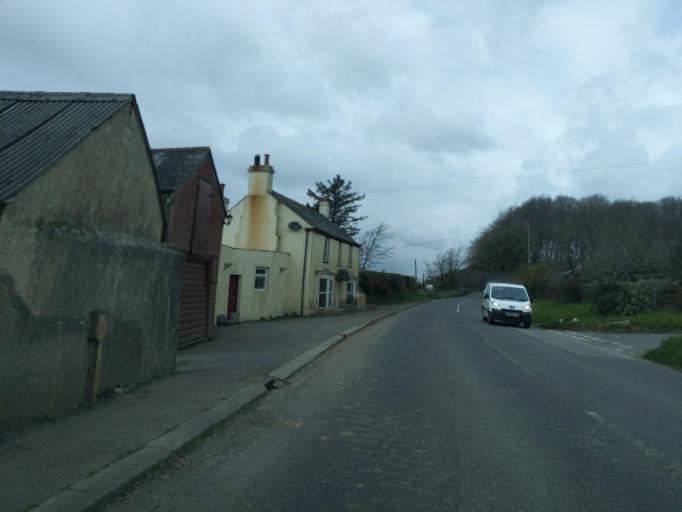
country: GB
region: England
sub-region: Cornwall
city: South Hill
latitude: 50.5349
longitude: -4.3367
